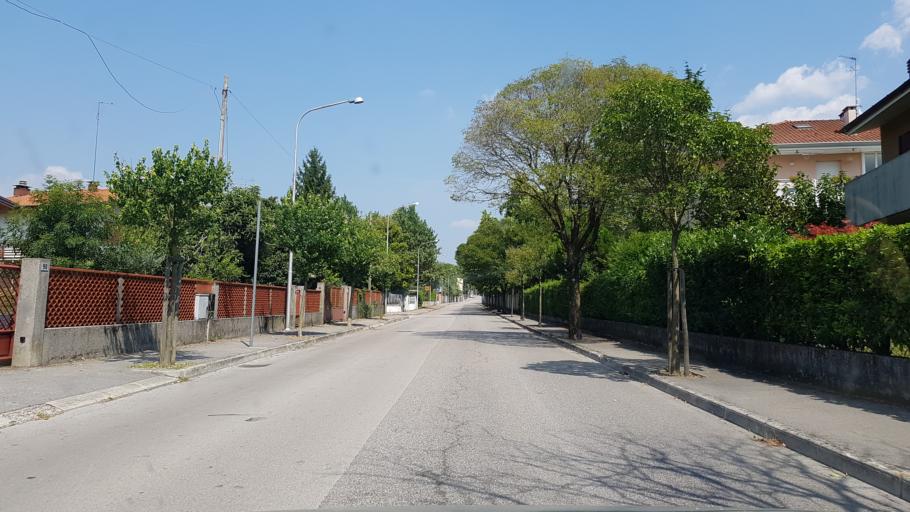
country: IT
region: Friuli Venezia Giulia
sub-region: Provincia di Gorizia
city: Gradisca d'Isonzo
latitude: 45.8869
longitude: 13.4909
